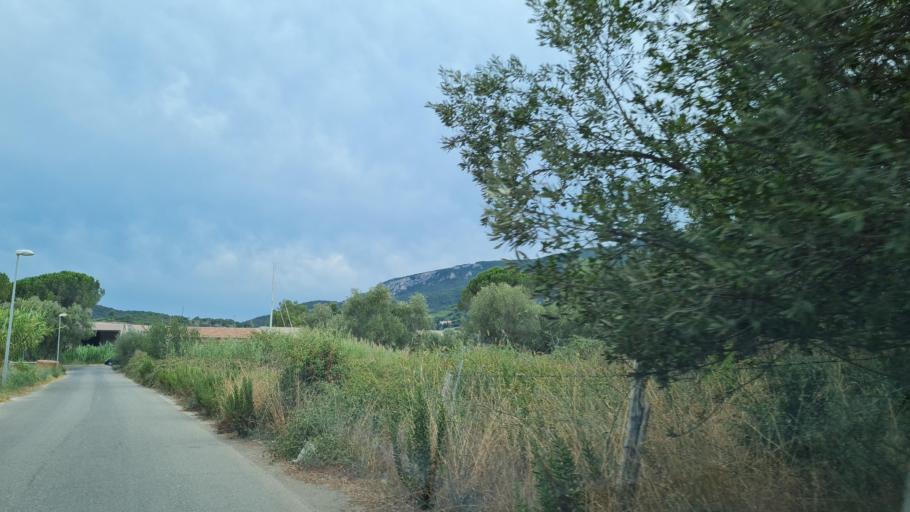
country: IT
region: Tuscany
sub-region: Provincia di Grosseto
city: Porto Ercole
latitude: 42.4038
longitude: 11.2038
